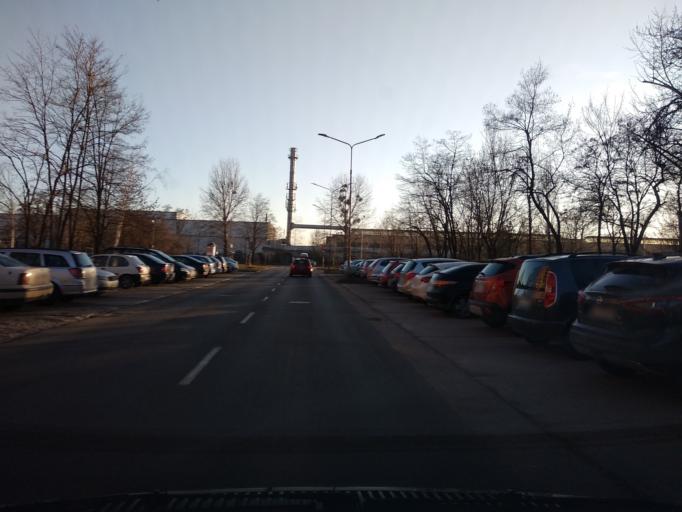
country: PL
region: Lower Silesian Voivodeship
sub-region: Powiat wroclawski
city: Wroclaw
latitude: 51.1228
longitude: 16.9670
